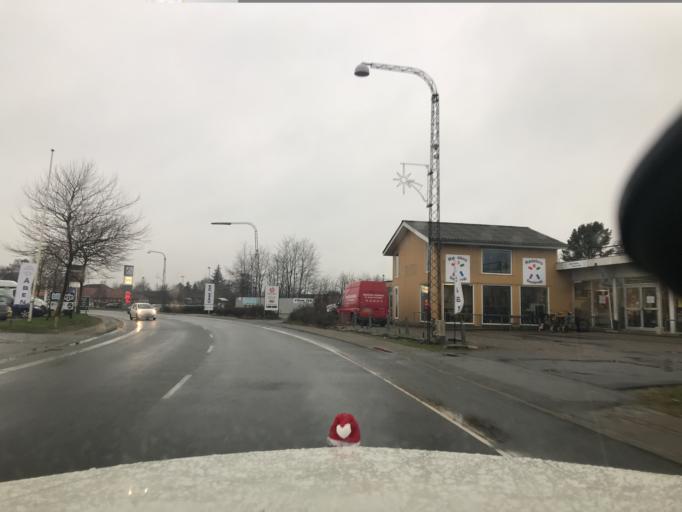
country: DK
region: South Denmark
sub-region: Aabenraa Kommune
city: Rodekro
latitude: 55.0700
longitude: 9.3489
